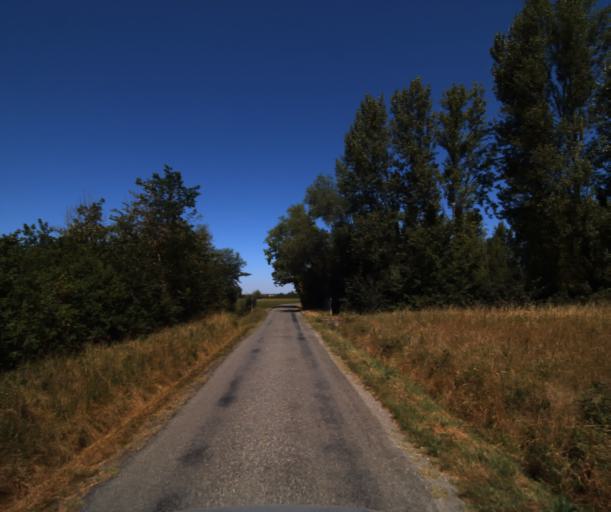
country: FR
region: Midi-Pyrenees
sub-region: Departement de la Haute-Garonne
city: Seysses
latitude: 43.4793
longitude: 1.2886
